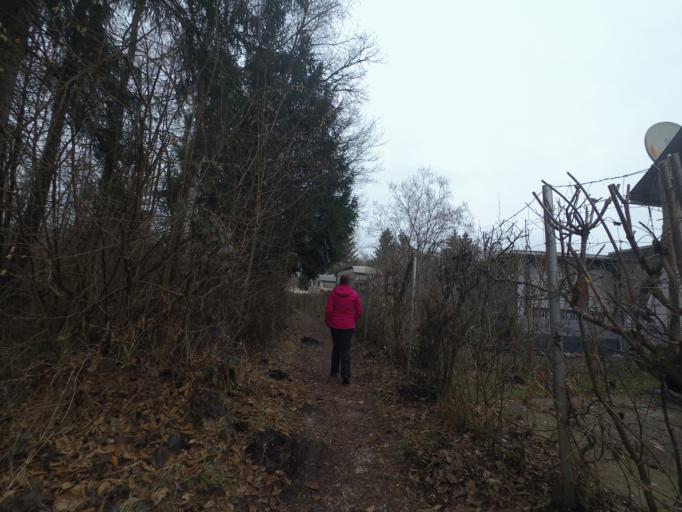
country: AT
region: Salzburg
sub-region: Politischer Bezirk Salzburg-Umgebung
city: Dorfbeuern
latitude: 48.0718
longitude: 12.9547
